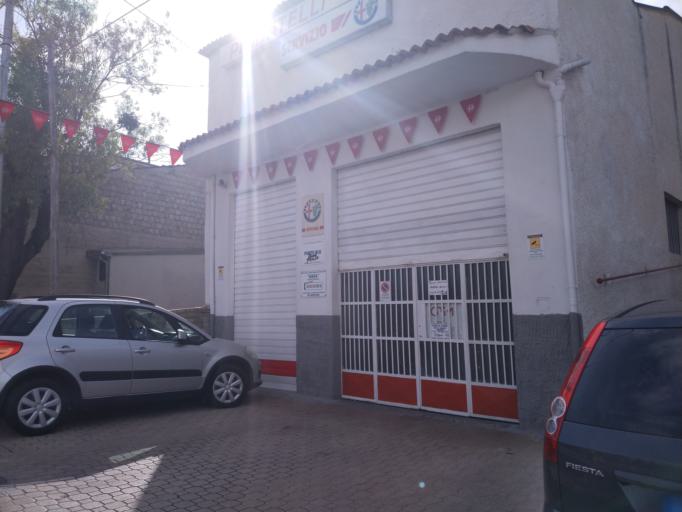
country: IT
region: Abruzzo
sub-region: Provincia dell' Aquila
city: Castelvecchio Subequo
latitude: 42.1318
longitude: 13.7316
